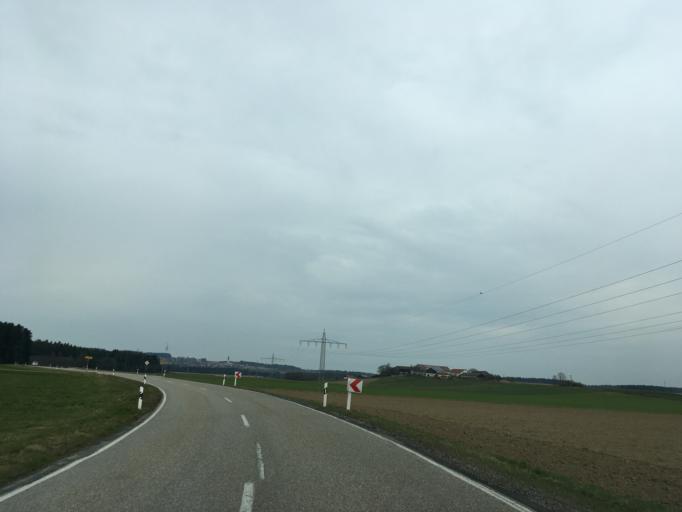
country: DE
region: Bavaria
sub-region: Upper Bavaria
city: Schnaitsee
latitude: 48.0365
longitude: 12.3724
